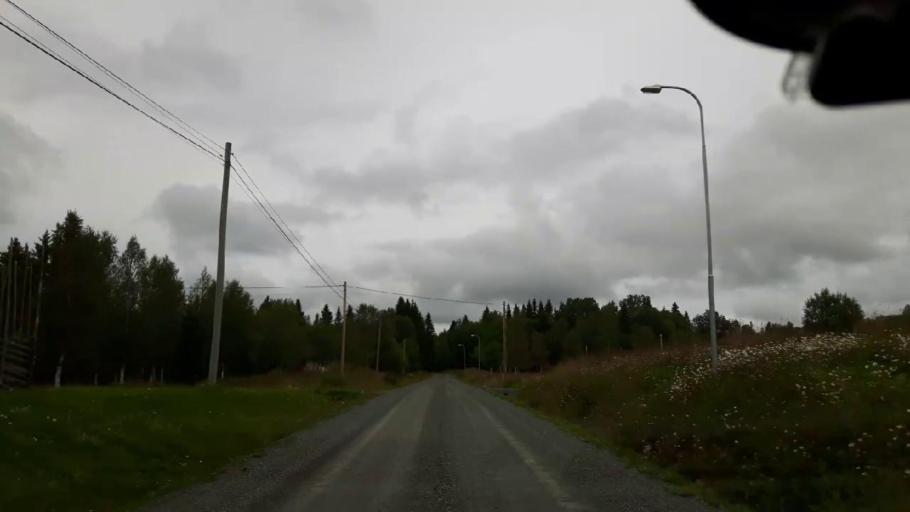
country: SE
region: Jaemtland
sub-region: Krokoms Kommun
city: Valla
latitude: 63.6993
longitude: 13.8727
